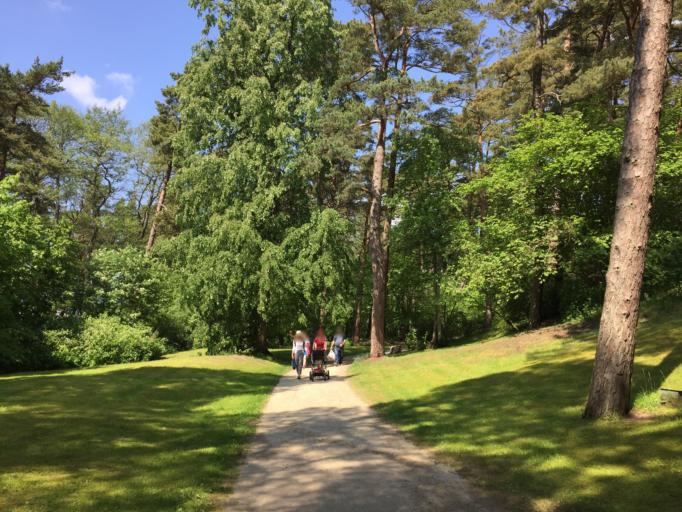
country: LT
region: Klaipedos apskritis
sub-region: Klaipeda
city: Palanga
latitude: 55.9052
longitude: 21.0525
